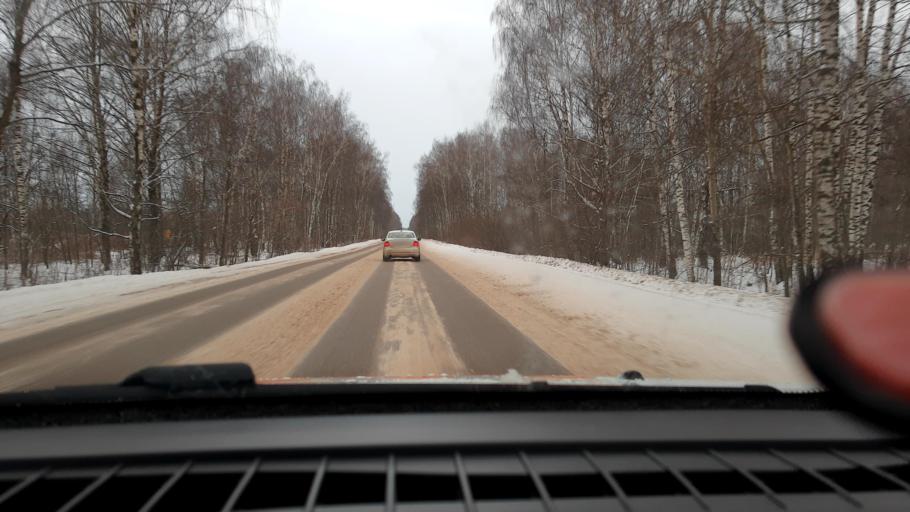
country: RU
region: Nizjnij Novgorod
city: Afonino
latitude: 56.3176
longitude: 44.1991
